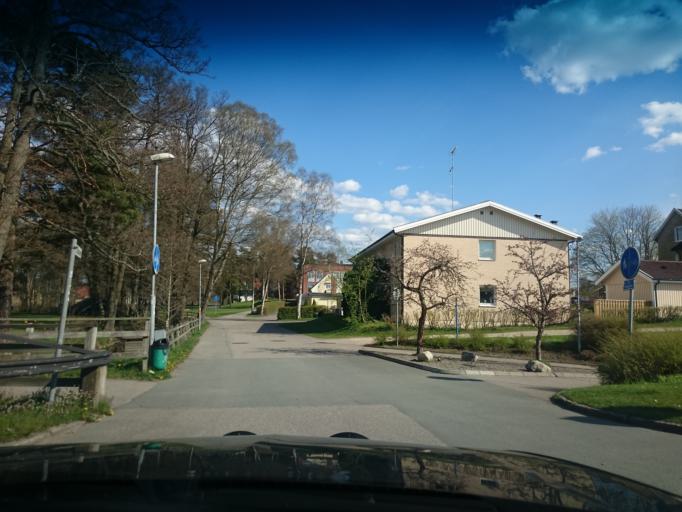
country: SE
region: Joenkoeping
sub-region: Vetlanda Kommun
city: Vetlanda
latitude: 57.4301
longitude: 15.0838
